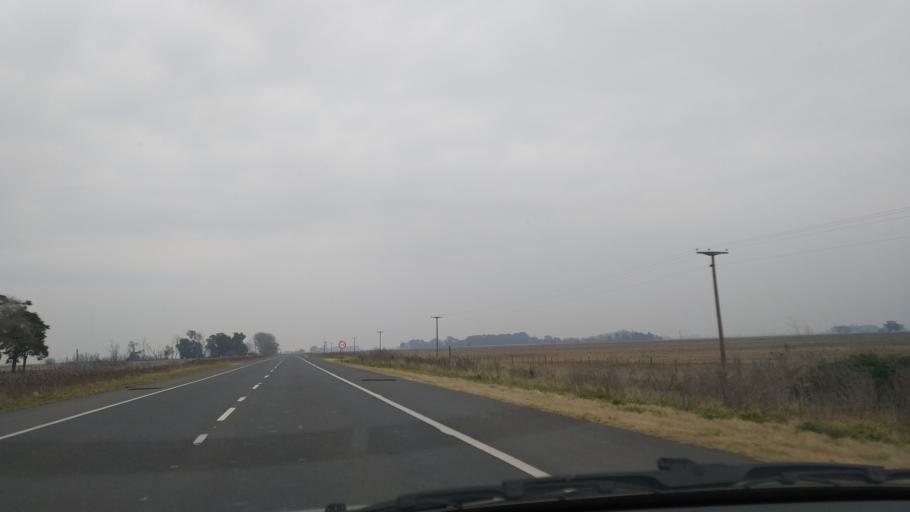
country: AR
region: Buenos Aires
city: Olavarria
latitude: -36.9963
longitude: -60.3358
